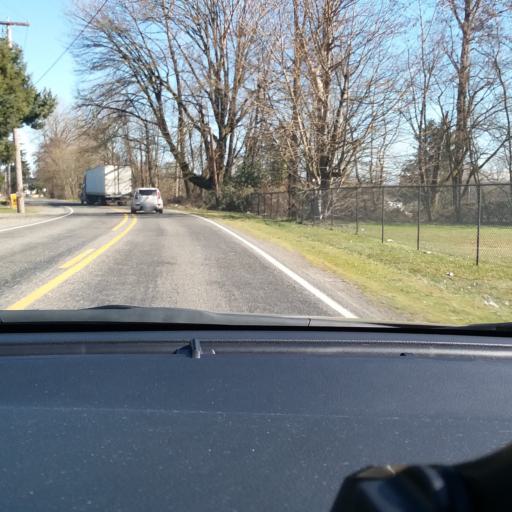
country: US
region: Washington
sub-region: Pierce County
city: Sumner
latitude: 47.2038
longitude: -122.2594
